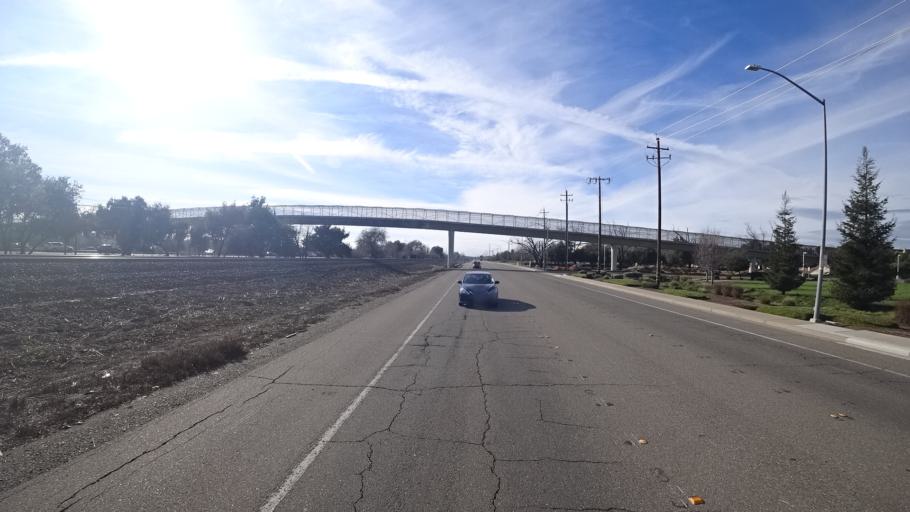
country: US
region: California
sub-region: Yolo County
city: Davis
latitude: 38.5508
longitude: -121.7072
